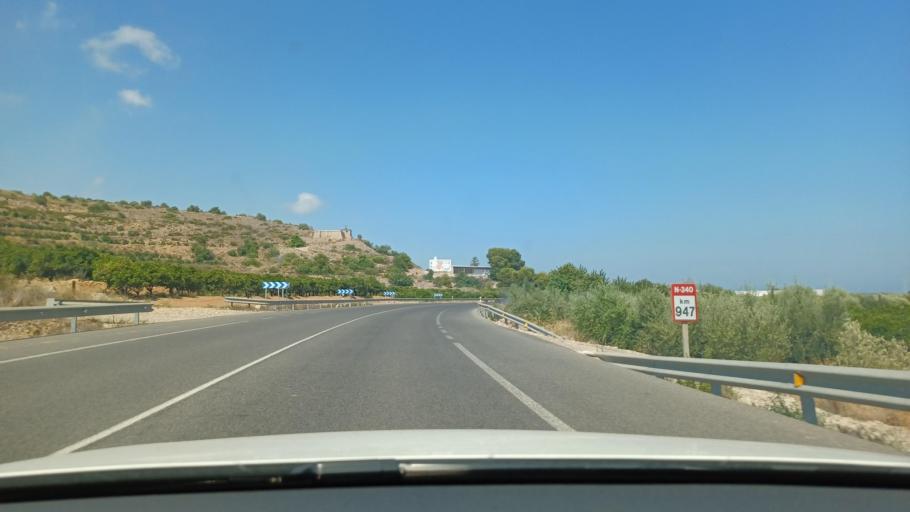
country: ES
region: Valencia
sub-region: Provincia de Castello
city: Chilches
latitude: 39.7747
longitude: -0.2021
